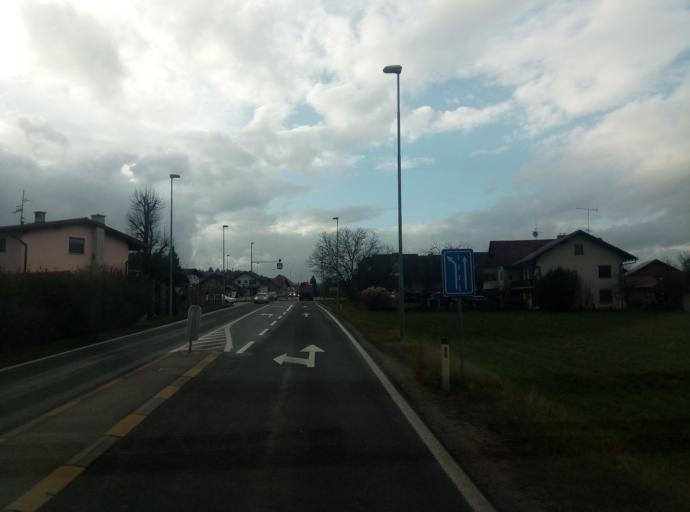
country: SI
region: Lukovica
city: Lukovica pri Domzalah
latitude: 46.1620
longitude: 14.6649
